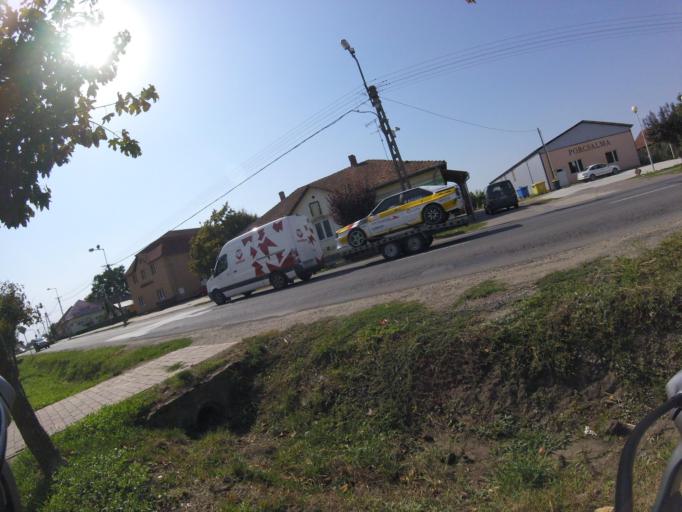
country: HU
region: Szabolcs-Szatmar-Bereg
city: Porcsalma
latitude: 47.8828
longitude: 22.5677
